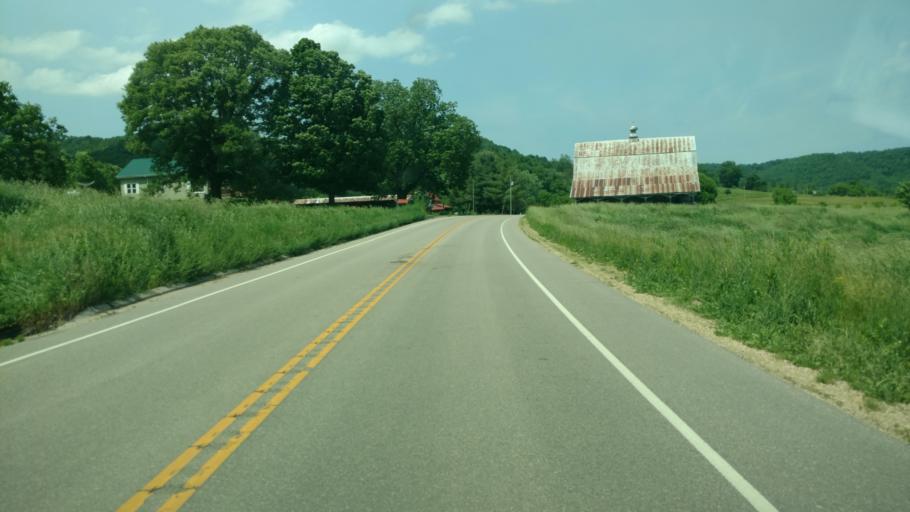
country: US
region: Wisconsin
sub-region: Vernon County
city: Viroqua
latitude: 43.5244
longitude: -90.6684
